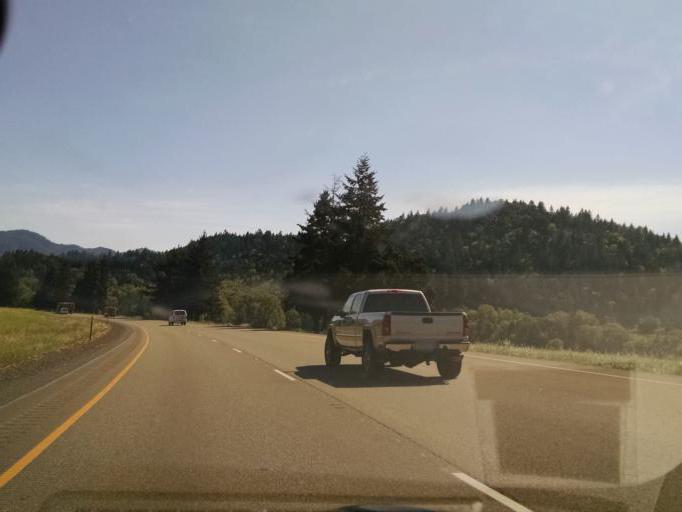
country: US
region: Oregon
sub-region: Douglas County
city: Tri-City
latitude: 42.9697
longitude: -123.3373
